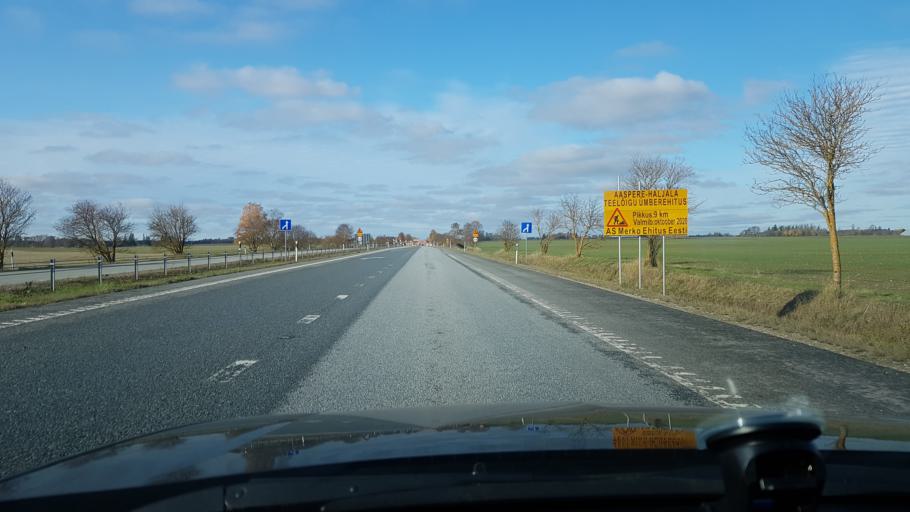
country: EE
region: Laeaene-Virumaa
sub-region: Haljala vald
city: Haljala
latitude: 59.4261
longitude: 26.2506
